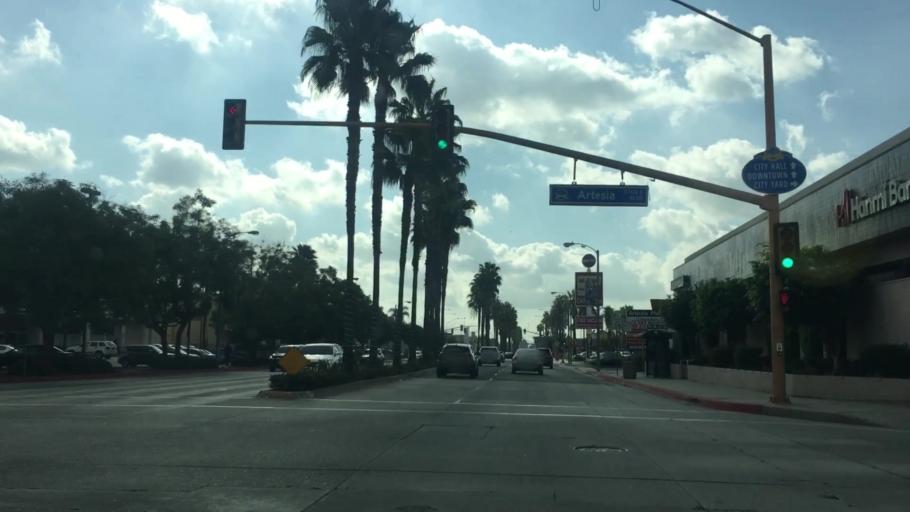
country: US
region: California
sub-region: Los Angeles County
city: Artesia
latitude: 33.8730
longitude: -118.0824
